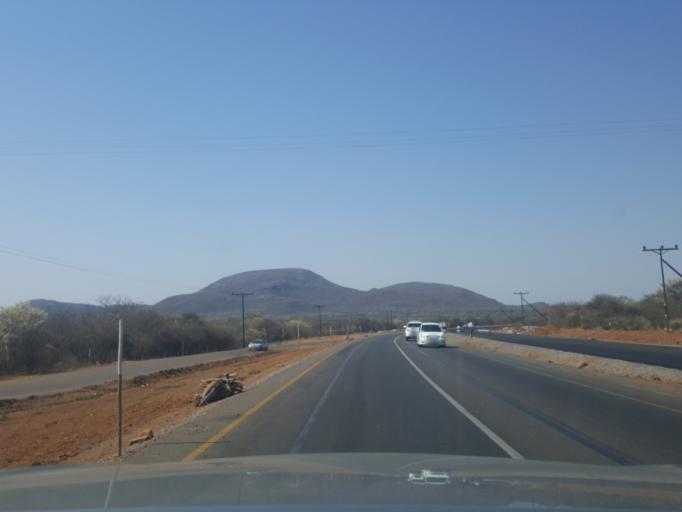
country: BW
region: Kweneng
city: Gabane
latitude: -24.7456
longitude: 25.8305
